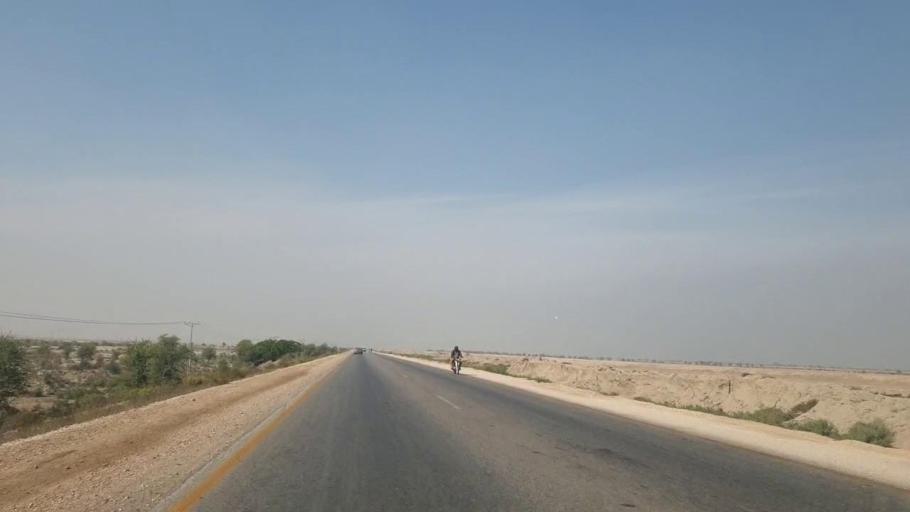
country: PK
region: Sindh
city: Sann
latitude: 25.9066
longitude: 68.2281
